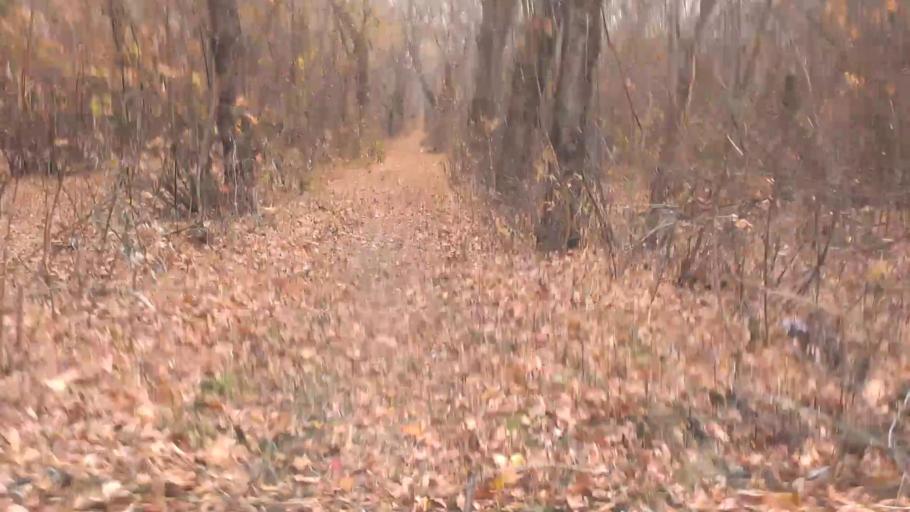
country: RU
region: Altai Krai
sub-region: Gorod Barnaulskiy
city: Barnaul
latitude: 53.3656
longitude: 83.7275
